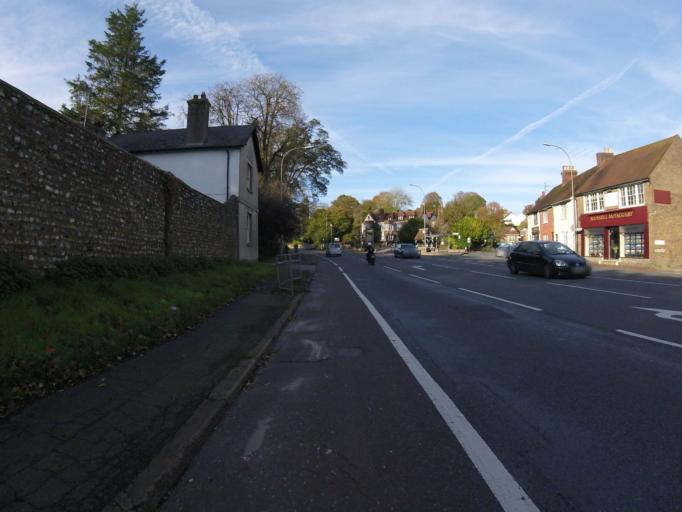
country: GB
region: England
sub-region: Brighton and Hove
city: Hove
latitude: 50.8645
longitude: -0.1522
